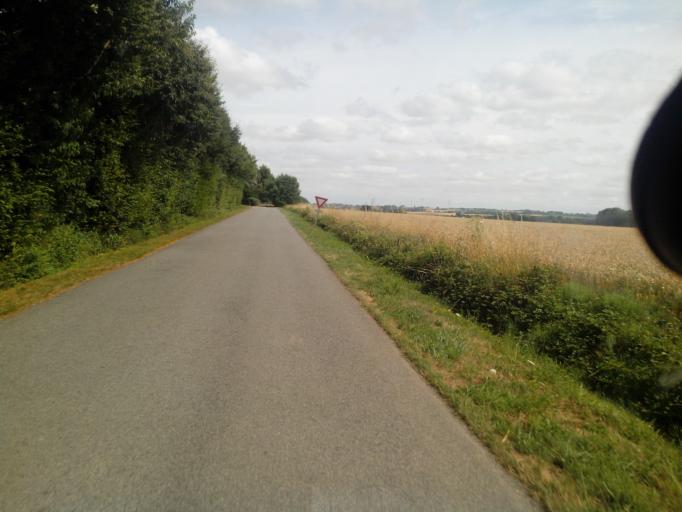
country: FR
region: Brittany
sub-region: Departement d'Ille-et-Vilaine
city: Messac
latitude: 47.8139
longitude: -1.8087
